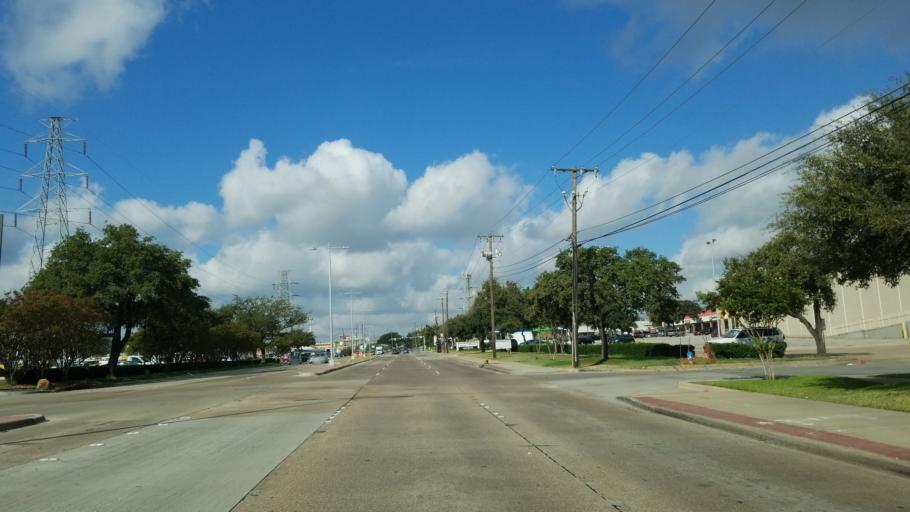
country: US
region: Texas
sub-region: Dallas County
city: Richardson
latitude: 32.9400
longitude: -96.7661
